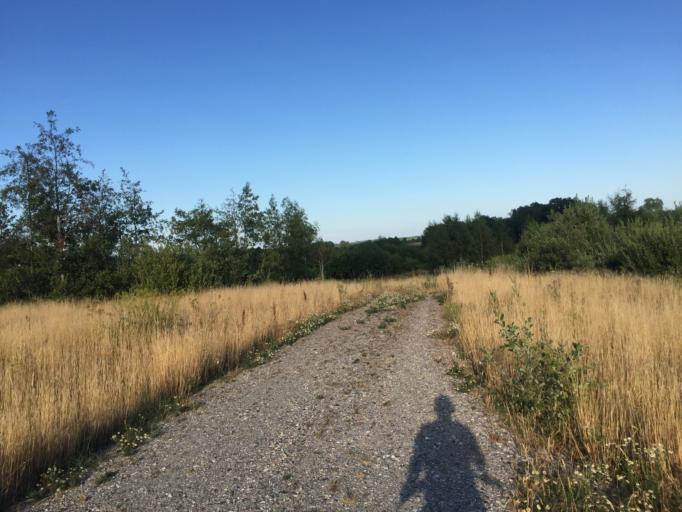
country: DK
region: South Denmark
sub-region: Odense Kommune
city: Bellinge
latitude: 55.3760
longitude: 10.2998
